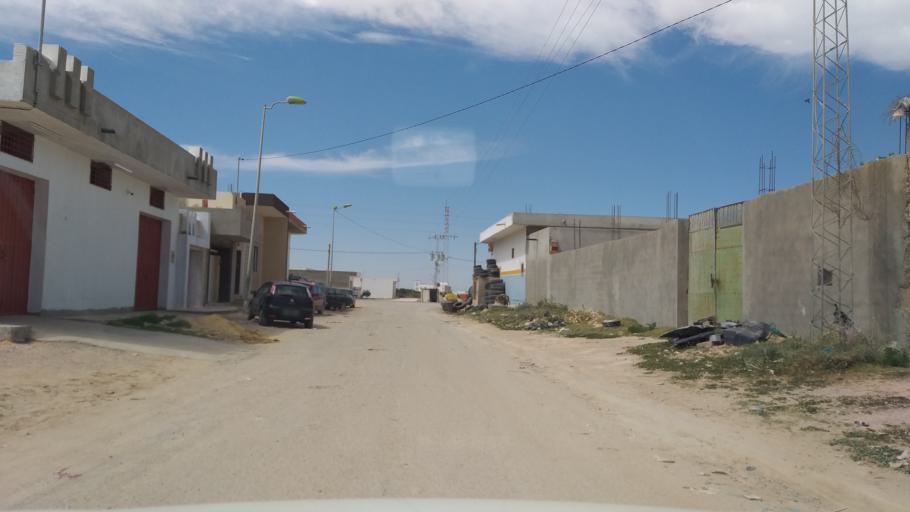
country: TN
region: Al Mahdiyah
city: El Jem
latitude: 35.3052
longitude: 10.6927
